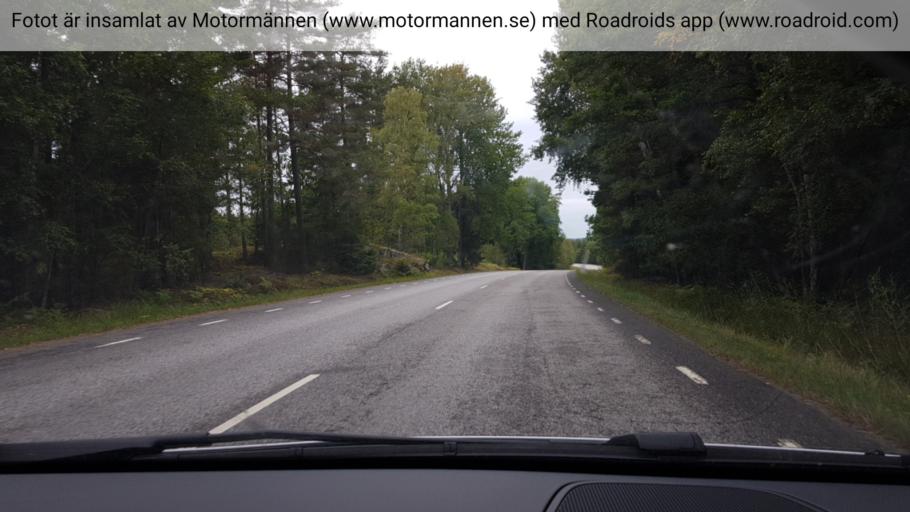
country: SE
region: Soedermanland
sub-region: Strangnas Kommun
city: Mariefred
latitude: 59.2375
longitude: 17.1963
